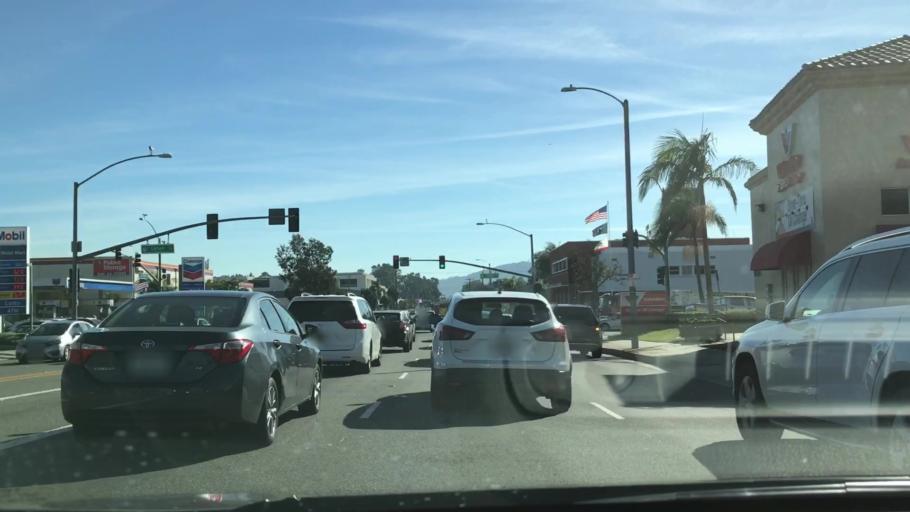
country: US
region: California
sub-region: Los Angeles County
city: Torrance
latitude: 33.8319
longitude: -118.3287
